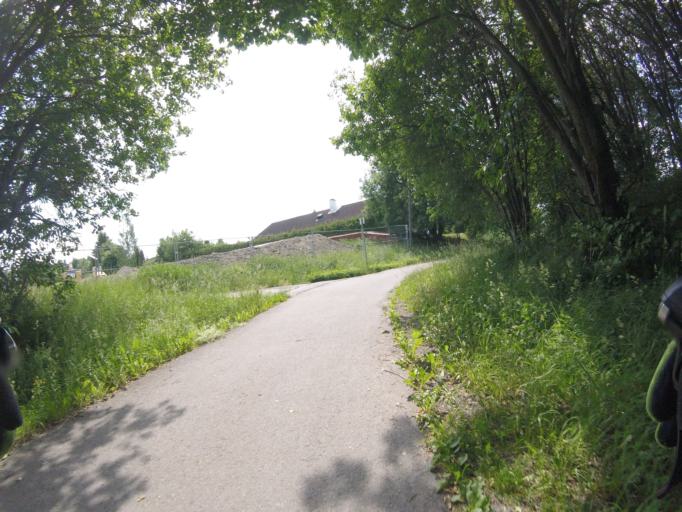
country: NO
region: Akershus
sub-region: Skedsmo
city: Lillestrom
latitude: 59.9734
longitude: 11.0558
